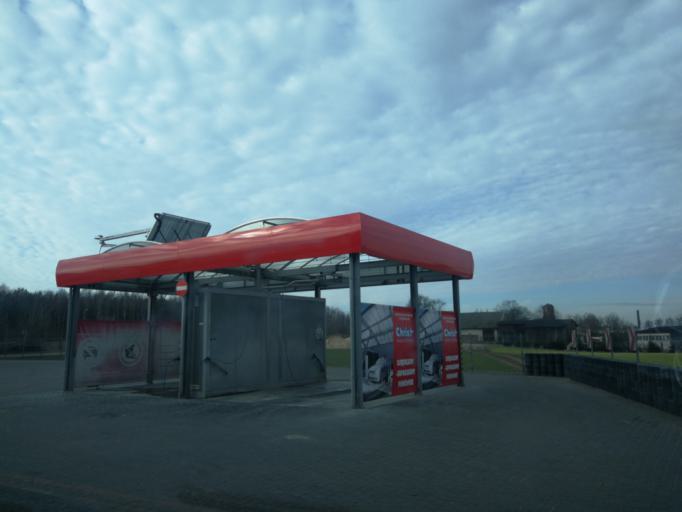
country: PL
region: Warmian-Masurian Voivodeship
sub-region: Powiat dzialdowski
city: Lidzbark
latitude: 53.2622
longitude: 19.8508
